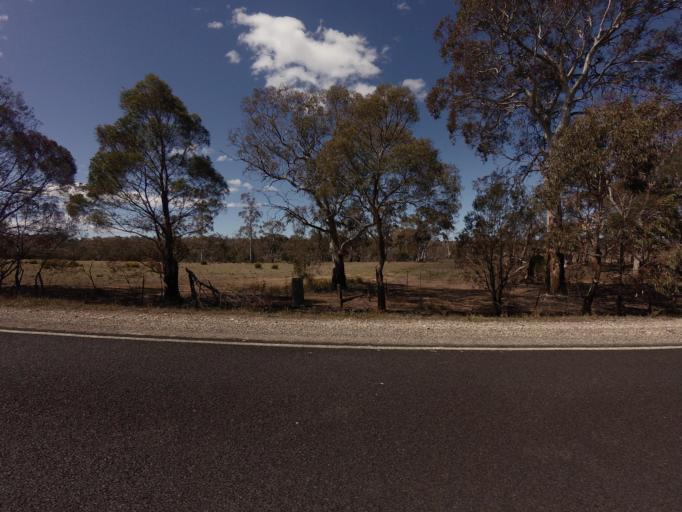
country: AU
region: Tasmania
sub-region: Break O'Day
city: St Helens
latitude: -42.0380
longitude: 148.0276
